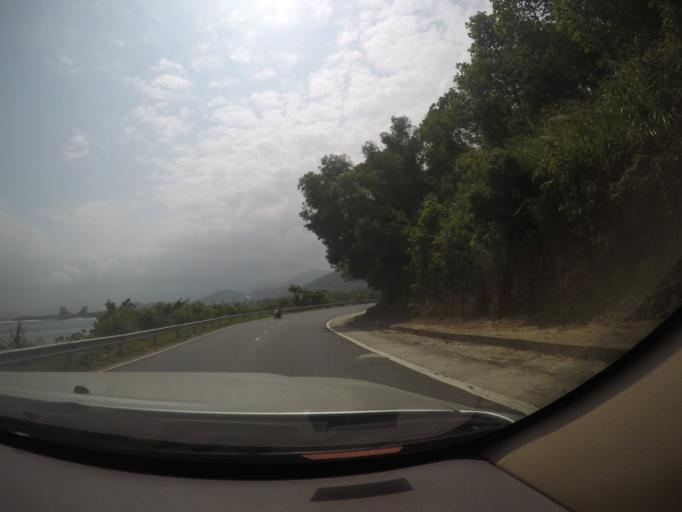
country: VN
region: Da Nang
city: Lien Chieu
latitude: 16.1432
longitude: 108.1289
